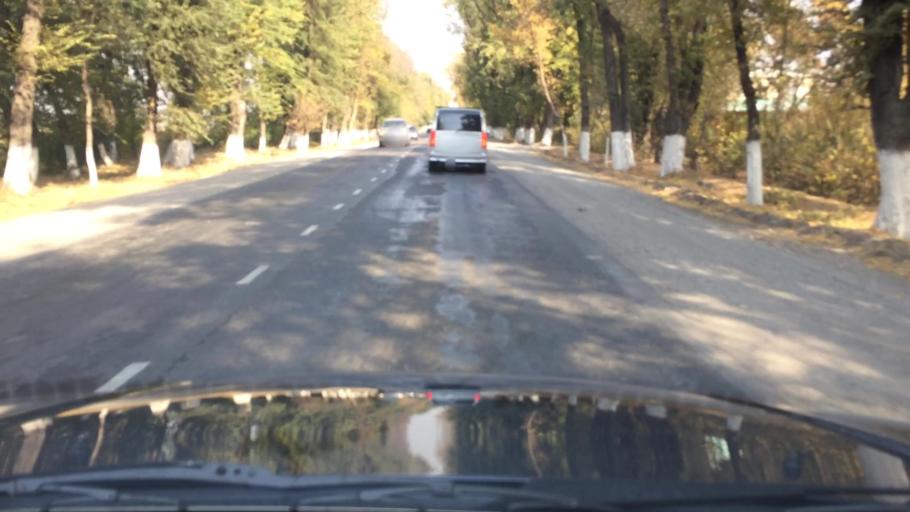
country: KG
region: Chuy
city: Lebedinovka
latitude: 42.9177
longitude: 74.6890
